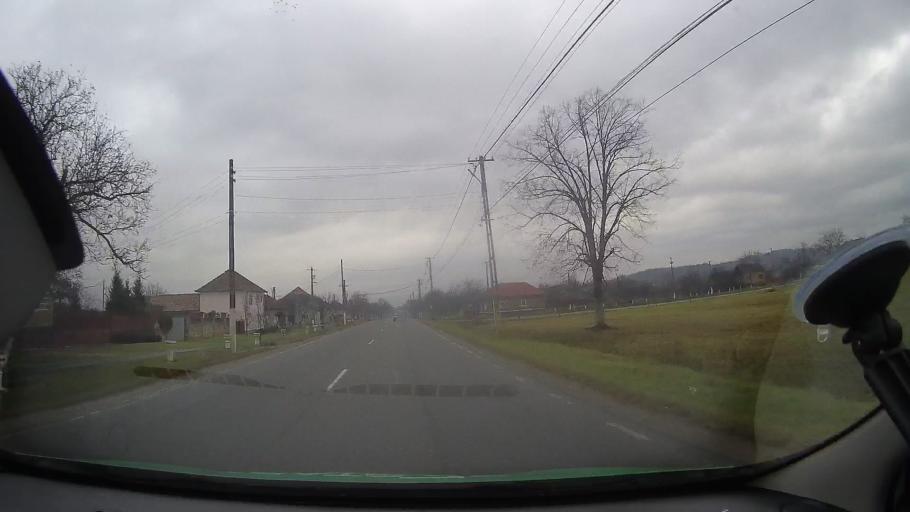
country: RO
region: Arad
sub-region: Comuna Almas
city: Almas
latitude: 46.2831
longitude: 22.2647
